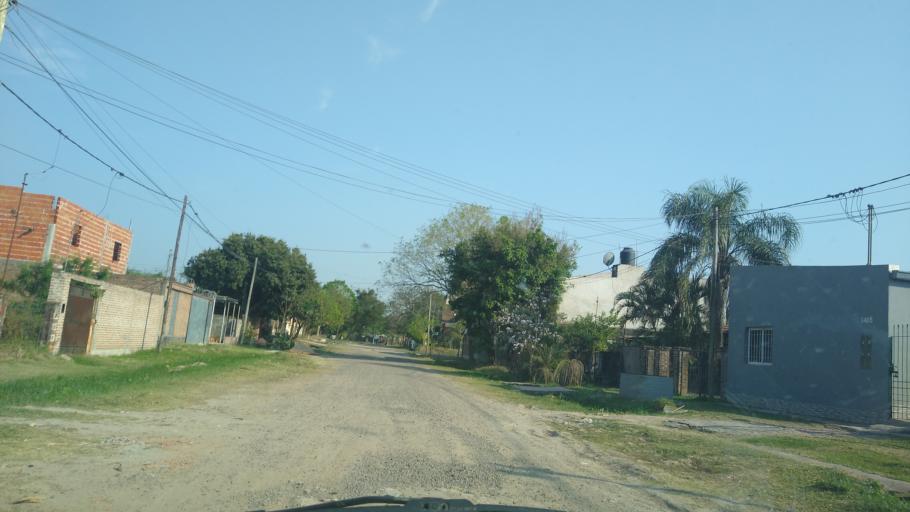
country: AR
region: Chaco
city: Barranqueras
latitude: -27.4757
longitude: -58.9519
